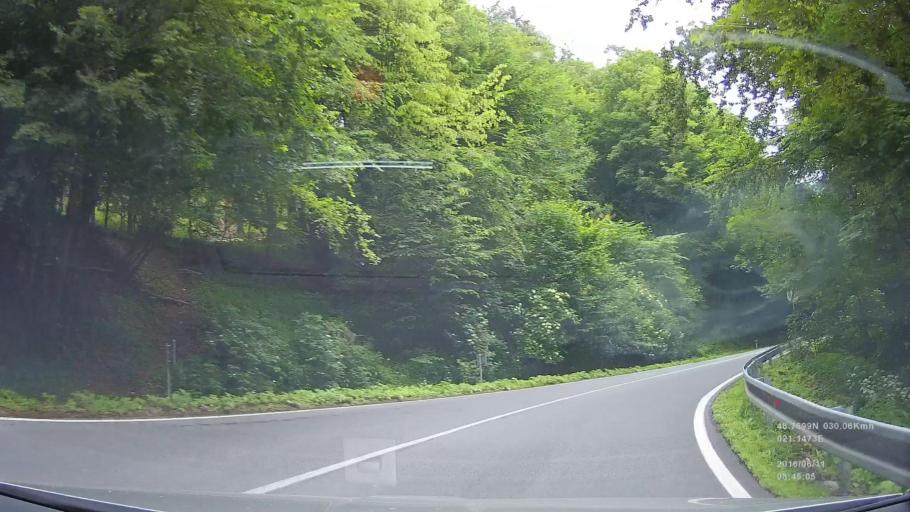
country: SK
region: Kosicky
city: Kosice
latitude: 48.7557
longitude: 21.1954
